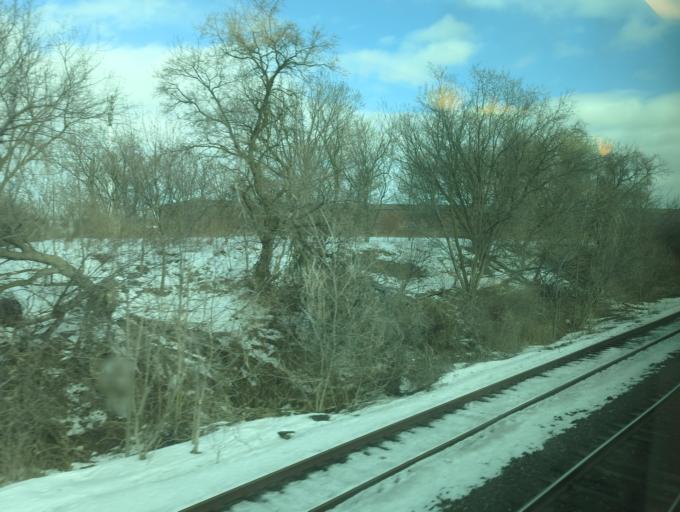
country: CA
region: Ontario
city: Etobicoke
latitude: 43.5960
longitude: -79.5375
